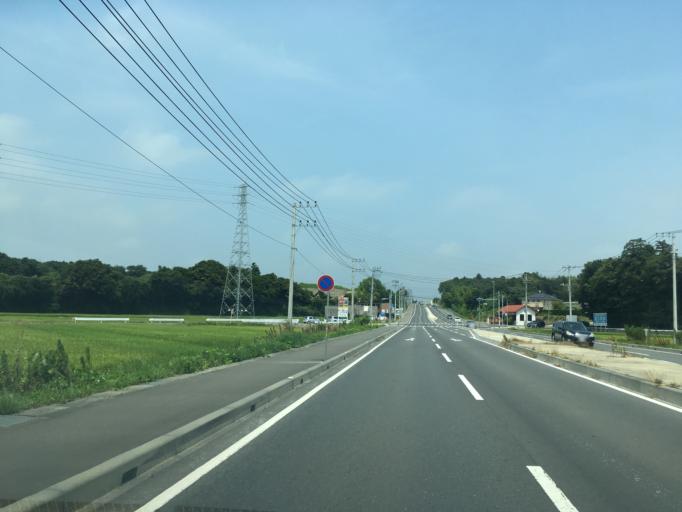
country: JP
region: Ibaraki
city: Oarai
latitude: 36.3623
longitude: 140.5793
